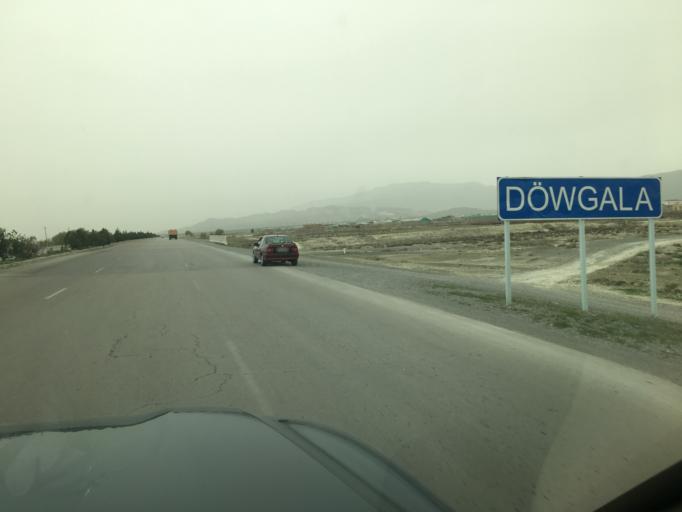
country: TM
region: Ahal
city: Baharly
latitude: 38.3084
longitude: 57.6174
